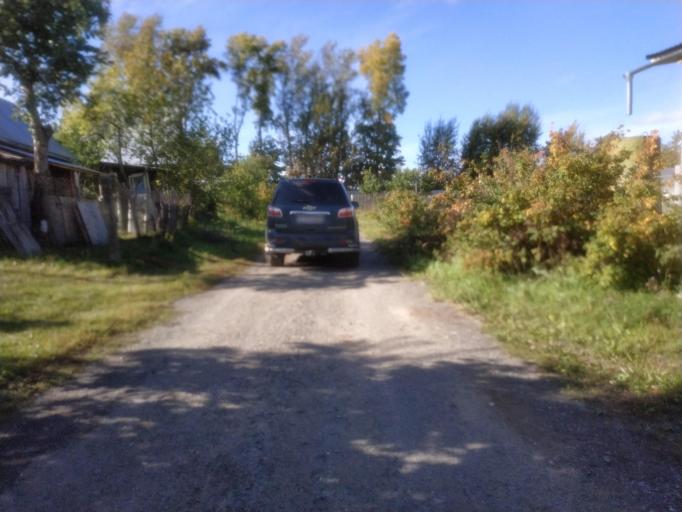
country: RU
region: Chuvashia
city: Novyye Lapsary
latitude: 56.1422
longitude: 47.1455
